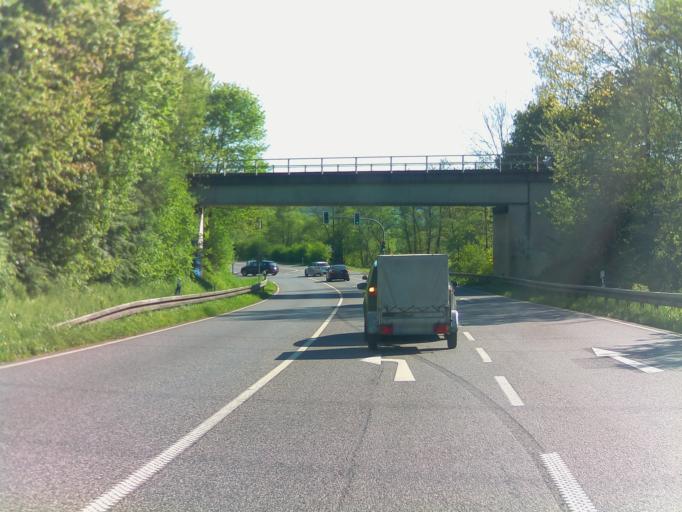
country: DE
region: Hesse
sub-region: Regierungsbezirk Darmstadt
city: Wachtersbach
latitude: 50.2408
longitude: 9.2910
